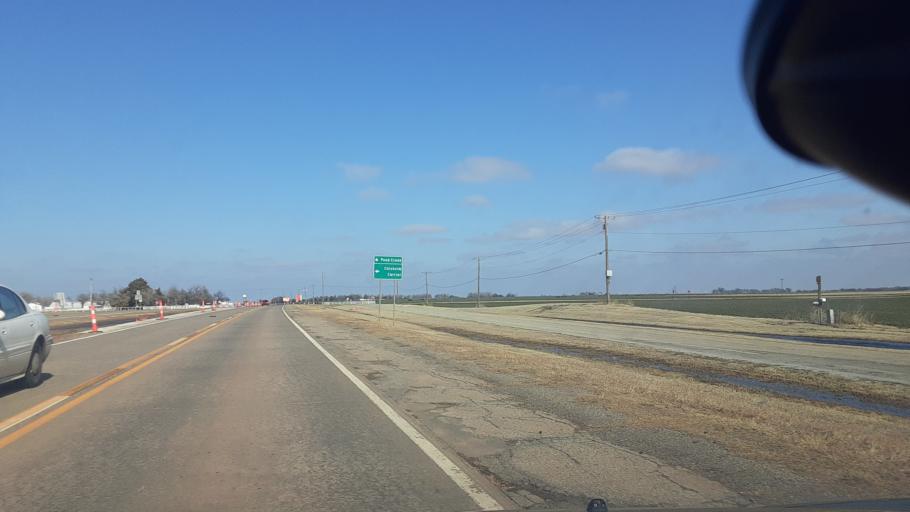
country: US
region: Oklahoma
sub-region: Garfield County
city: Enid
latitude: 36.4609
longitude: -97.8729
